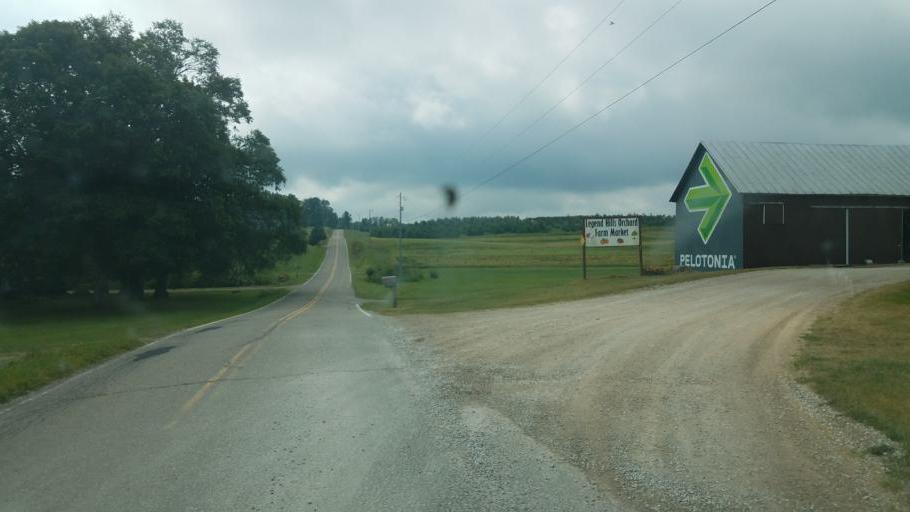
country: US
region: Ohio
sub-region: Licking County
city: Utica
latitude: 40.2171
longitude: -82.4585
